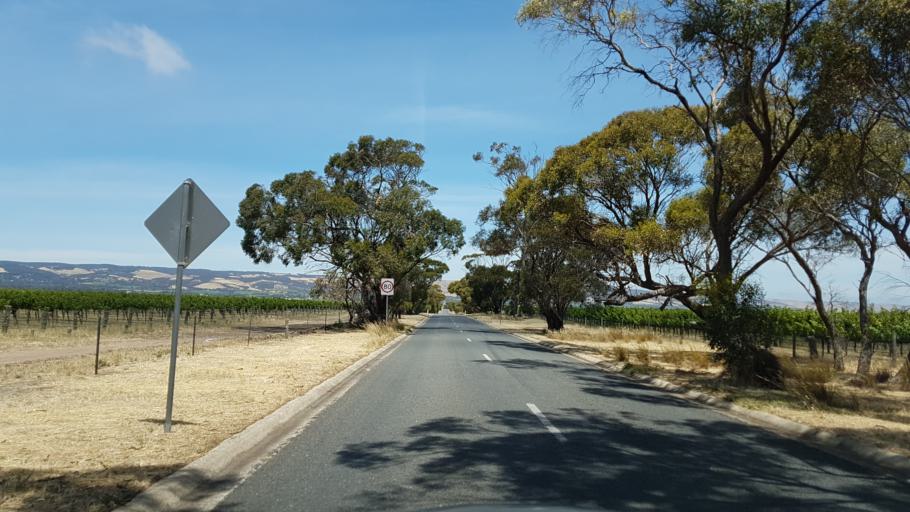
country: AU
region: South Australia
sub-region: Onkaparinga
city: McLaren Vale
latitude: -35.2325
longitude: 138.5192
